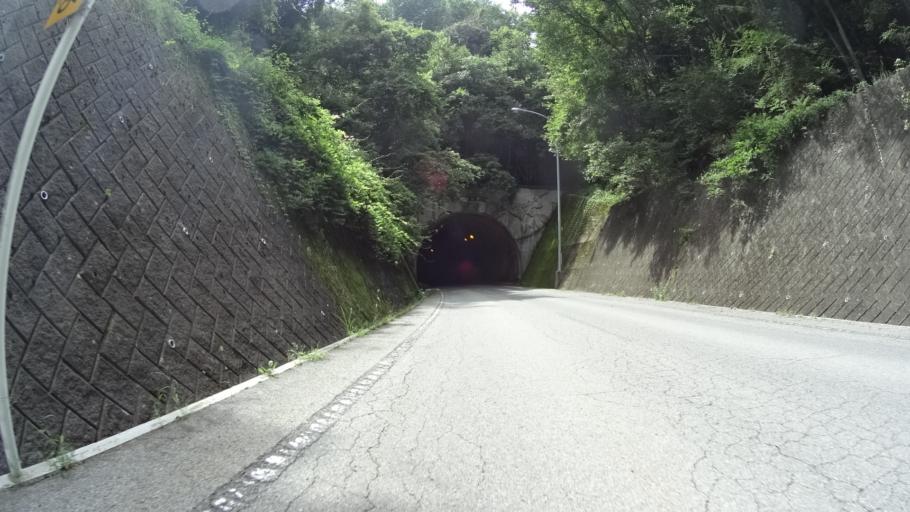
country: JP
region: Yamanashi
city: Nirasaki
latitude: 35.8702
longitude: 138.5057
